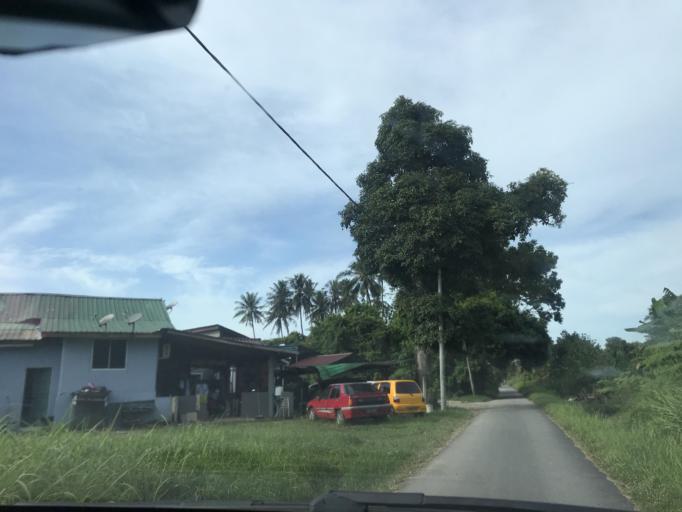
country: MY
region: Kelantan
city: Kota Bharu
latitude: 6.1354
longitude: 102.2203
